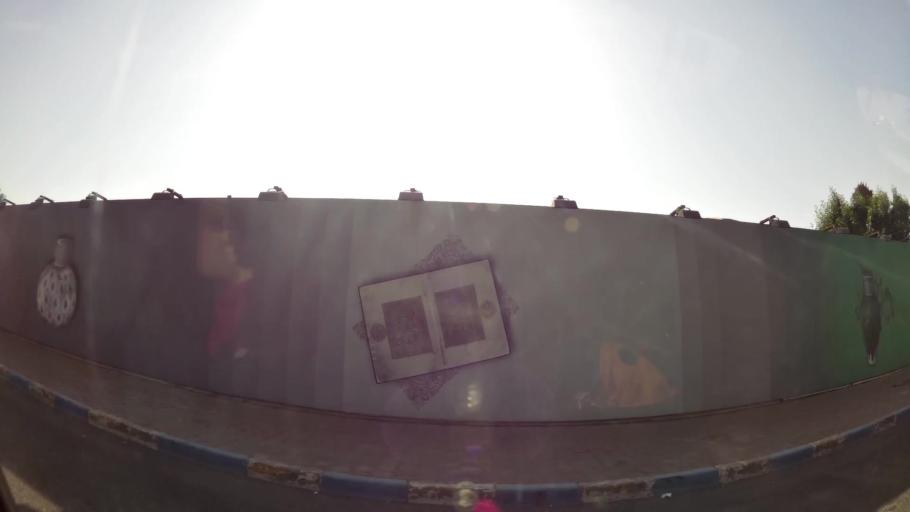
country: KW
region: Al Asimah
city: Kuwait City
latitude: 29.3741
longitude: 47.9662
